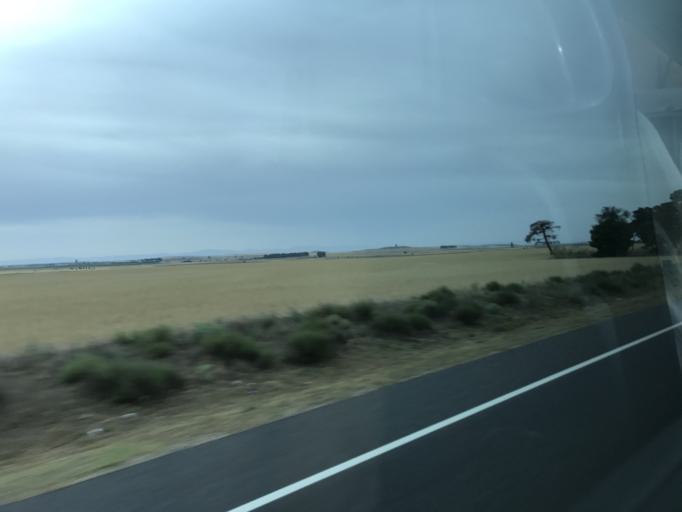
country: ES
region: Castille and Leon
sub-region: Provincia de Segovia
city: Rapariegos
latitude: 41.0728
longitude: -4.6338
